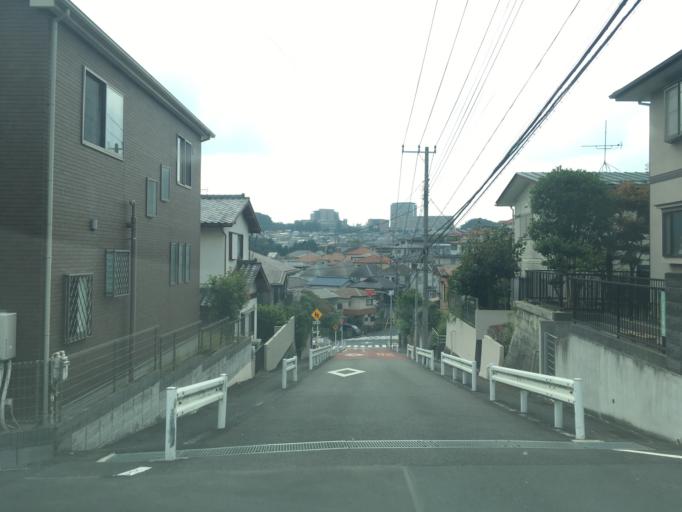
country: JP
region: Tokyo
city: Hino
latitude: 35.6547
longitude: 139.4063
